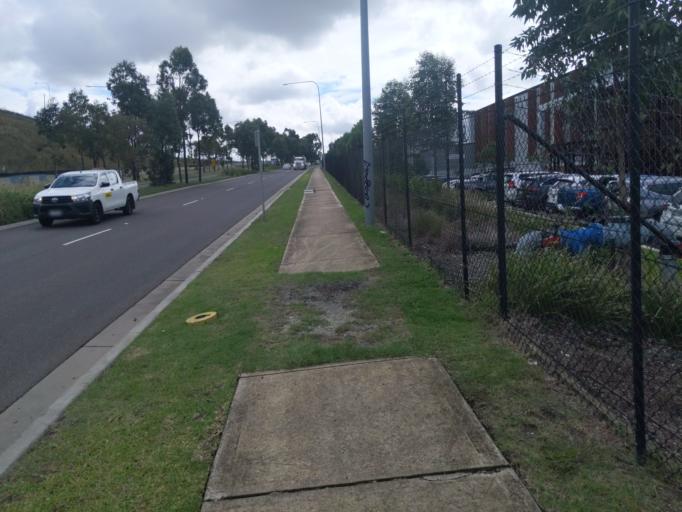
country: AU
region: New South Wales
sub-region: Holroyd
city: Girraween
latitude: -33.8207
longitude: 150.9188
